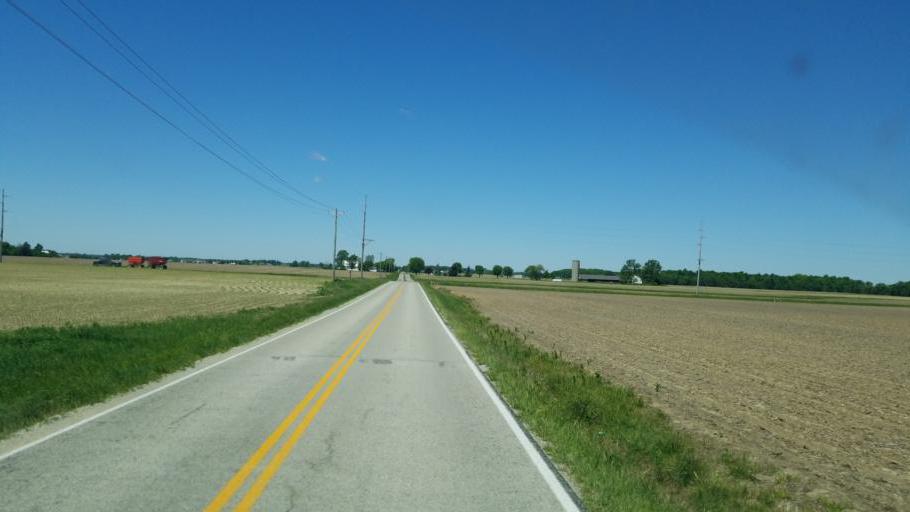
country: US
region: Ohio
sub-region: Shelby County
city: Anna
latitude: 40.3804
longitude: -84.2192
